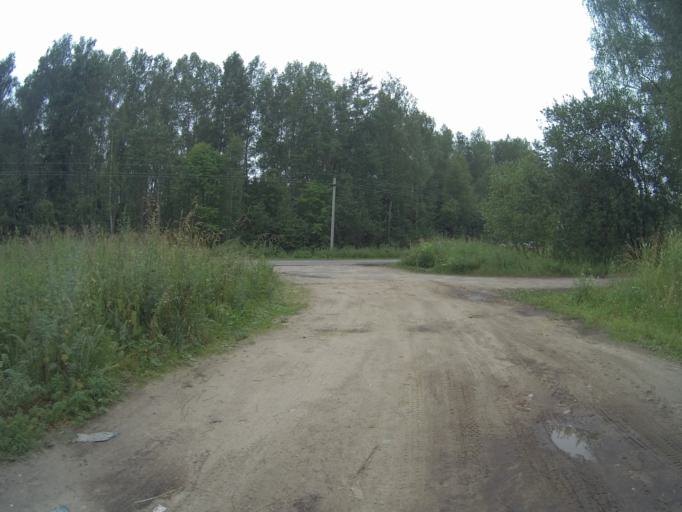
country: RU
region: Vladimir
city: Raduzhnyy
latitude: 55.9935
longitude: 40.2108
